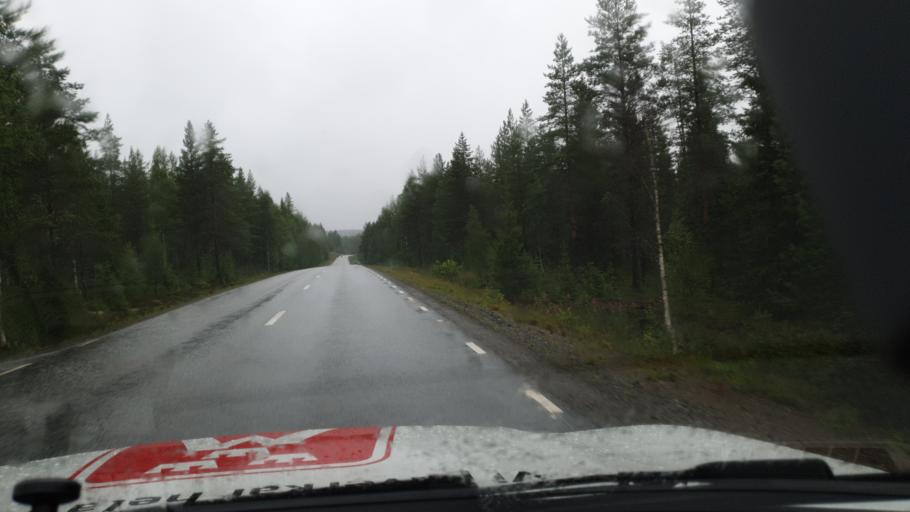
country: SE
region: Vaesterbotten
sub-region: Umea Kommun
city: Ersmark
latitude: 64.2814
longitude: 20.2244
